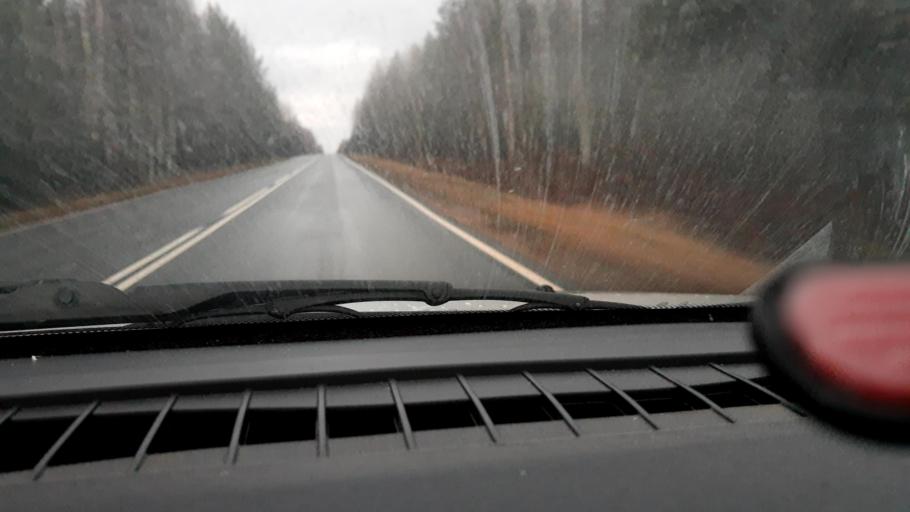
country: RU
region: Nizjnij Novgorod
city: Uren'
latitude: 57.2686
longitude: 45.6242
